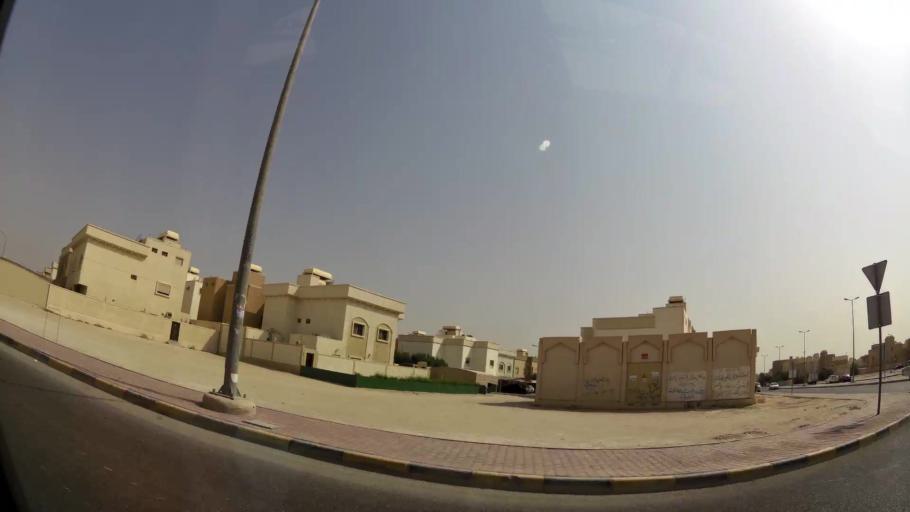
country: KW
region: Muhafazat al Jahra'
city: Al Jahra'
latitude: 29.3204
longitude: 47.7251
